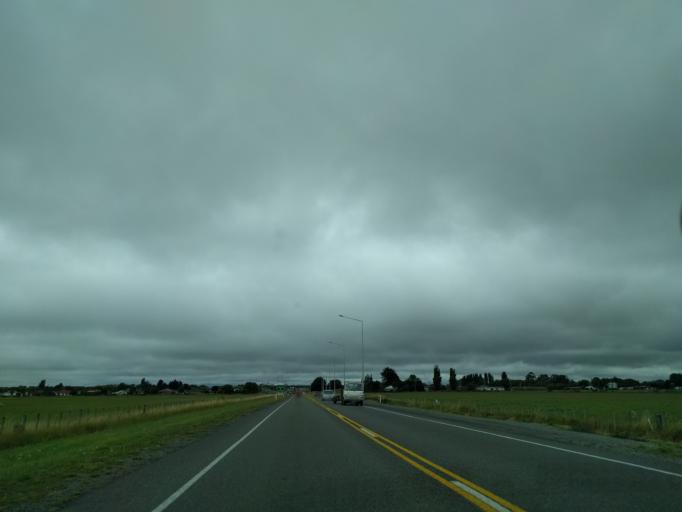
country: NZ
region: Canterbury
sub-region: Waimakariri District
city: Kaiapoi
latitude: -43.3688
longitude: 172.6492
